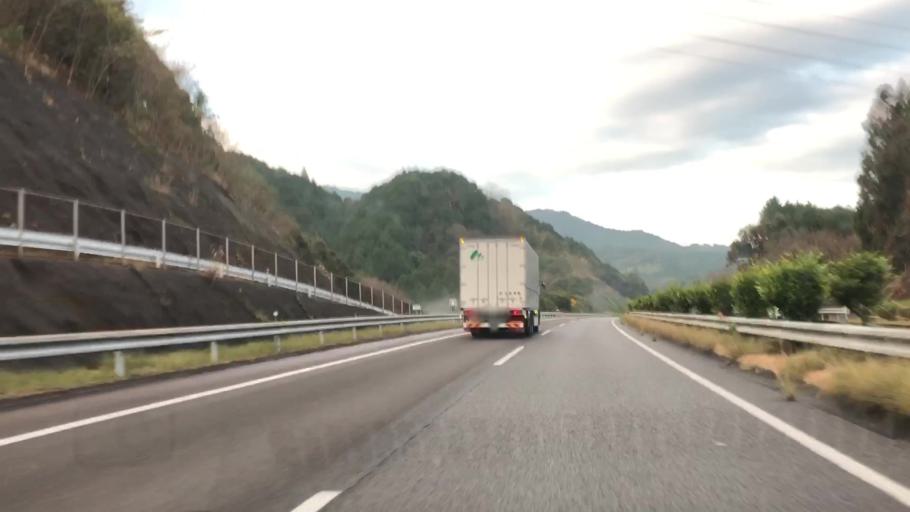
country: JP
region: Saga Prefecture
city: Takeocho-takeo
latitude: 33.1625
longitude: 130.0289
